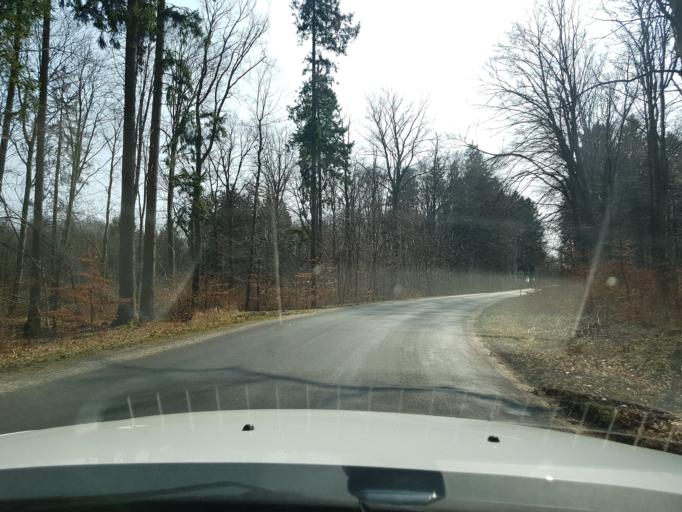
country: PL
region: West Pomeranian Voivodeship
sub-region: Powiat koszalinski
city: Sianow
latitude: 54.2603
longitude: 16.3146
